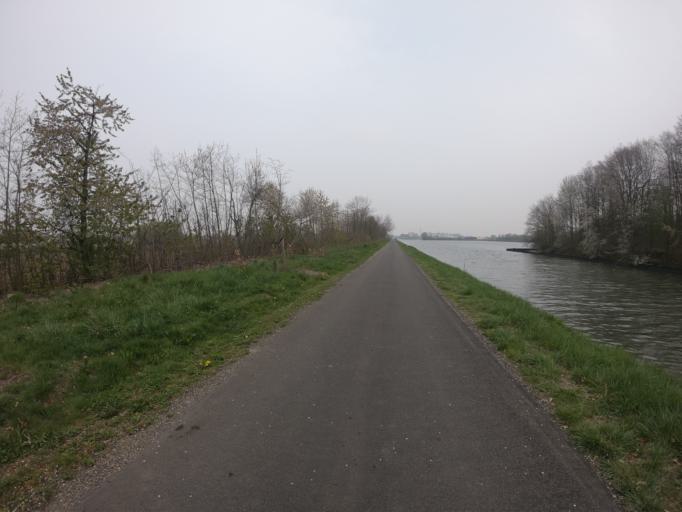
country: BE
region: Flanders
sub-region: Provincie Limburg
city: Maasmechelen
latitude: 50.9136
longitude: 5.6965
